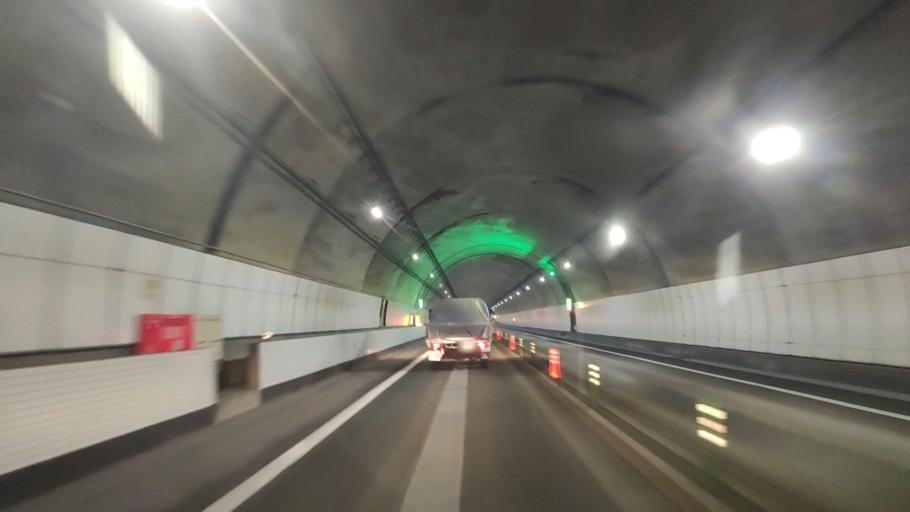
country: JP
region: Gifu
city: Takayama
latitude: 36.1931
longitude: 137.5696
